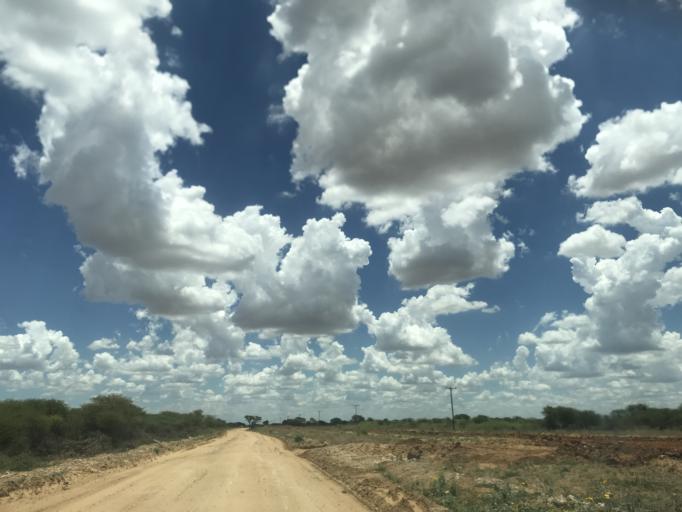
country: BW
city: Mabuli
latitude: -25.7911
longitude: 24.6523
